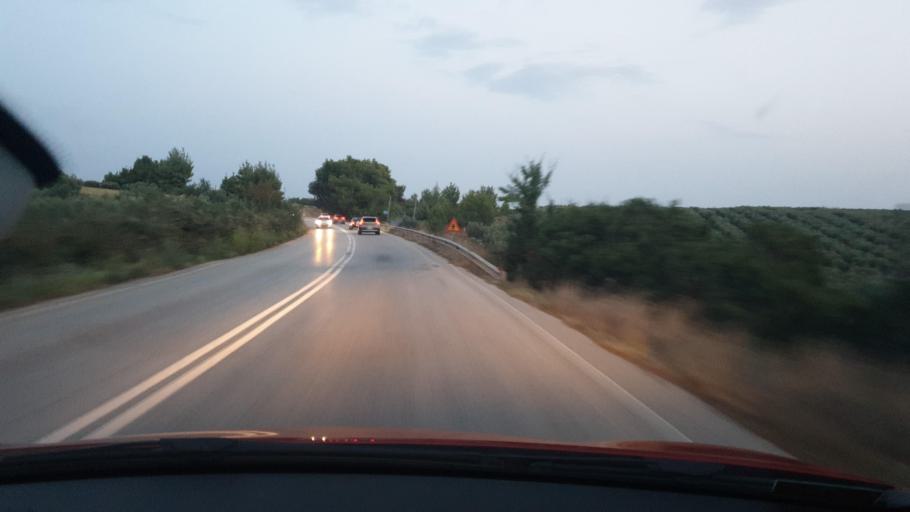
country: GR
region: Central Macedonia
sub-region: Nomos Chalkidikis
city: Ormylia
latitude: 40.2406
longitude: 23.5867
